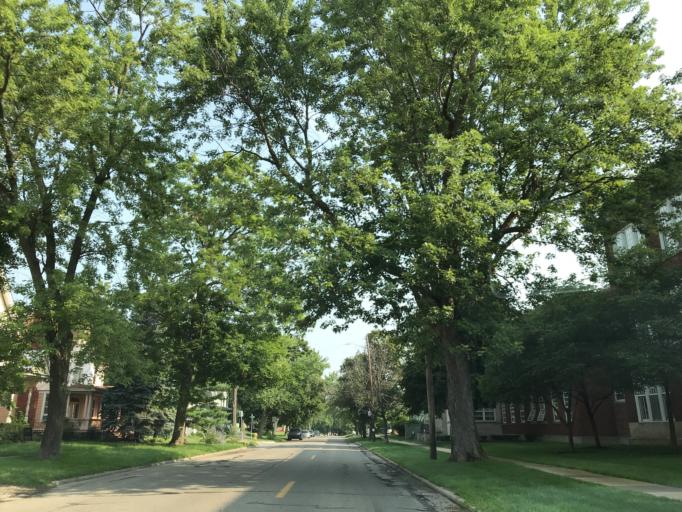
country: US
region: Michigan
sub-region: Washtenaw County
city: Ypsilanti
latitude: 42.2459
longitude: -83.6161
